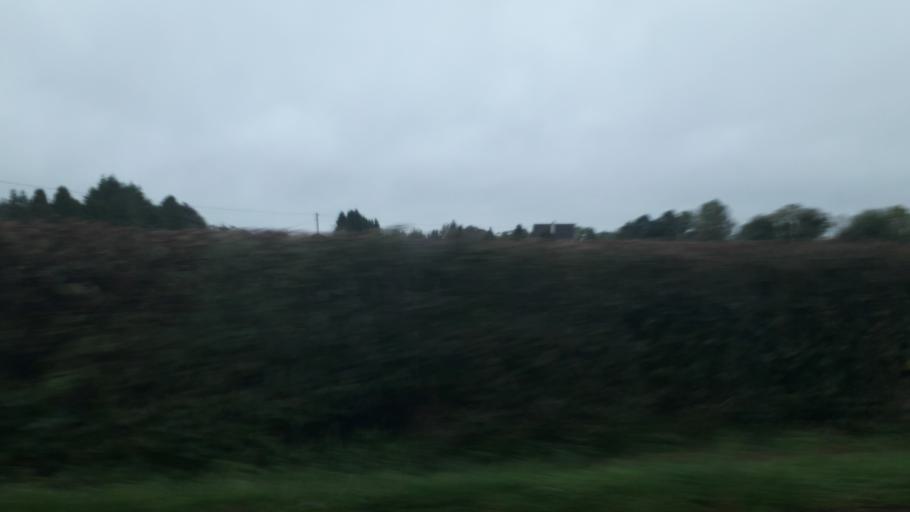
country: IE
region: Leinster
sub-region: An Iarmhi
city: An Muileann gCearr
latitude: 53.6222
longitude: -7.4601
